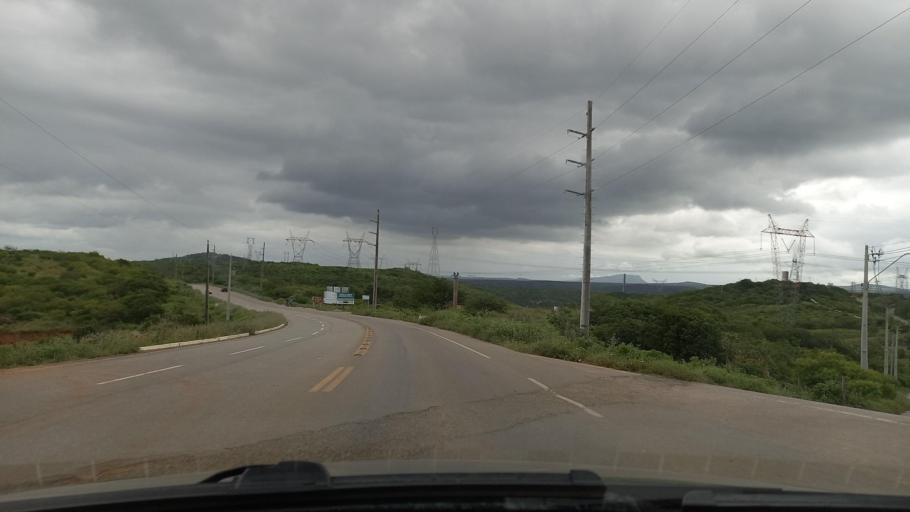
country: BR
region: Sergipe
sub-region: Caninde De Sao Francisco
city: Caninde de Sao Francisco
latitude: -9.6535
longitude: -37.7887
